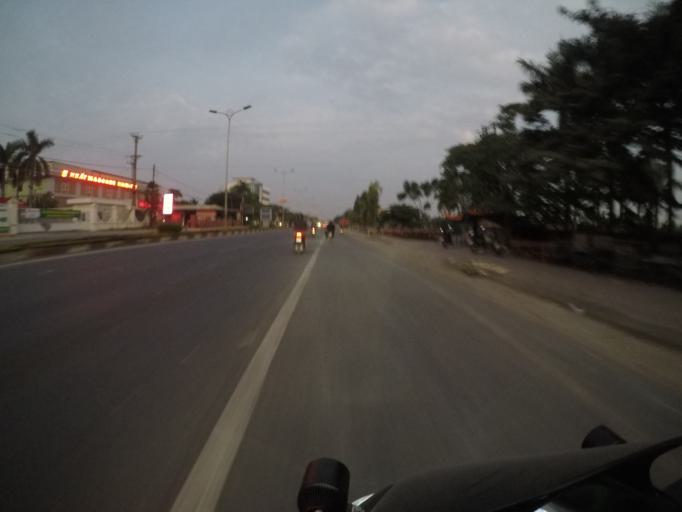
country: VN
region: Vinh Phuc
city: Phuc Yen
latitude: 21.2400
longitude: 105.7305
